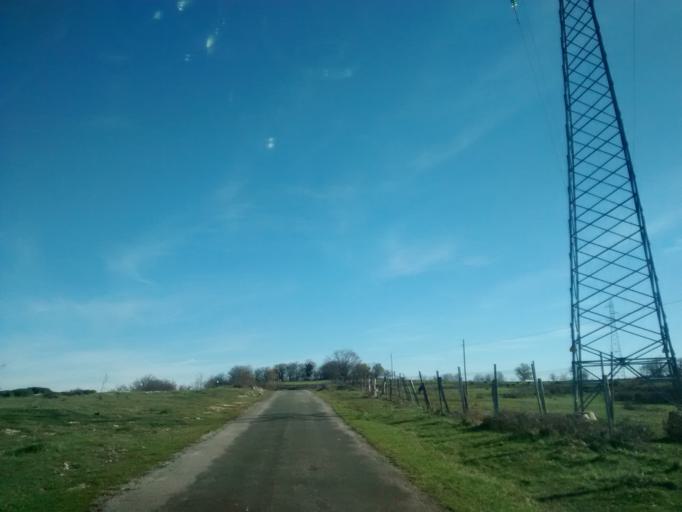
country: ES
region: Cantabria
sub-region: Provincia de Cantabria
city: San Pedro del Romeral
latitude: 42.9694
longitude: -3.7647
